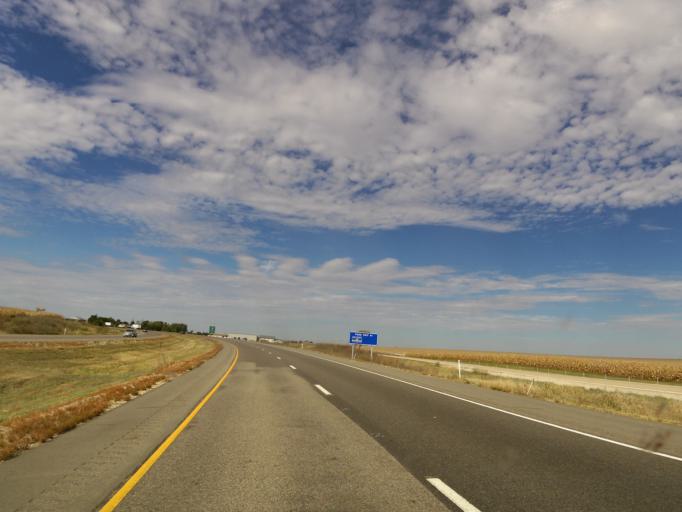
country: US
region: Illinois
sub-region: Marshall County
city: Wenona
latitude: 41.0976
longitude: -89.0672
